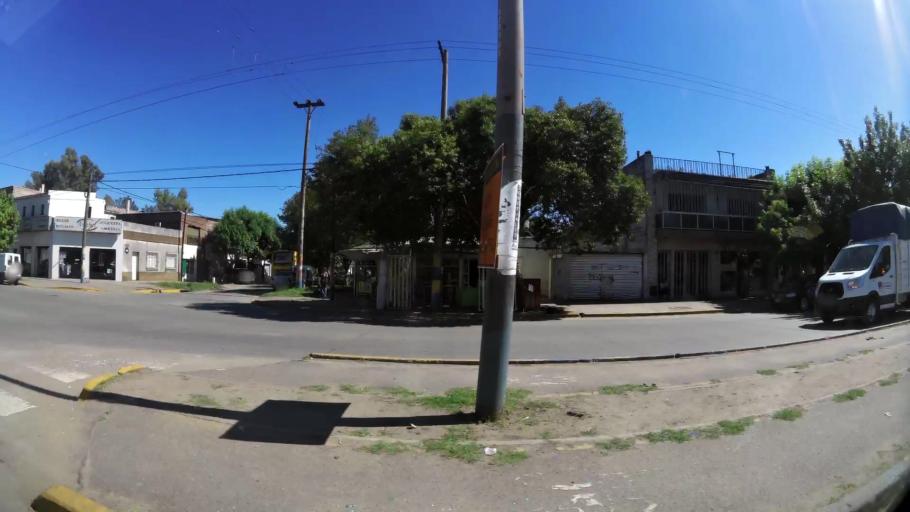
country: AR
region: Santa Fe
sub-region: Departamento de Rosario
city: Rosario
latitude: -32.9705
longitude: -60.6946
